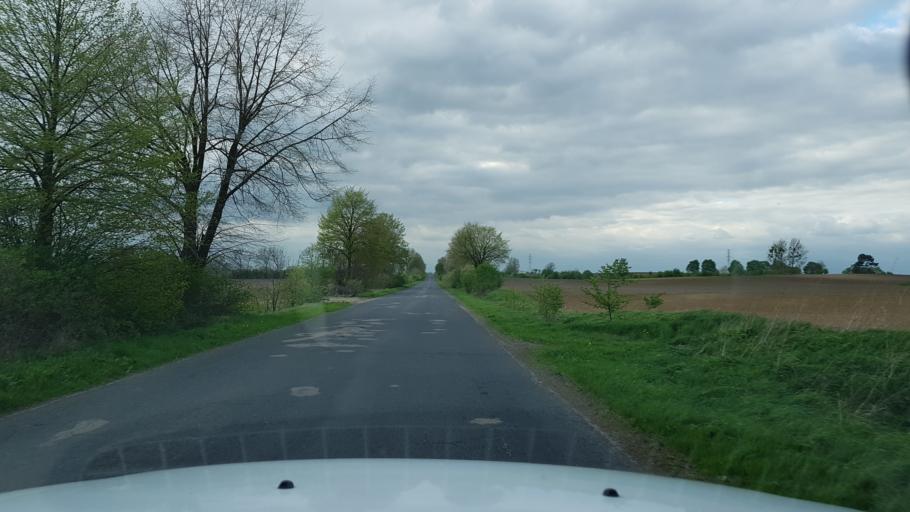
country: PL
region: West Pomeranian Voivodeship
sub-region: Powiat pyrzycki
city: Przelewice
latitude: 53.1391
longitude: 15.0299
